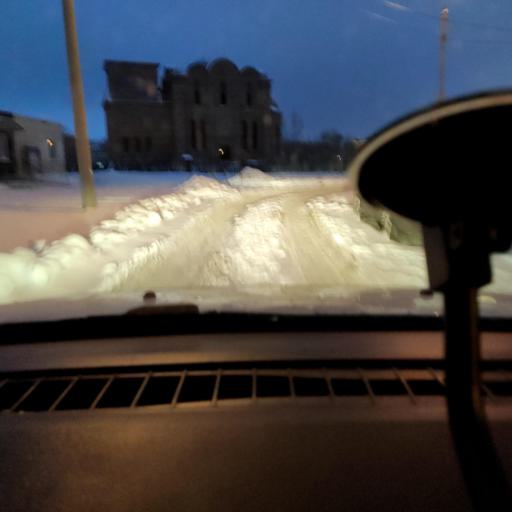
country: RU
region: Samara
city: Rozhdestveno
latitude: 53.1412
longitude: 50.0454
